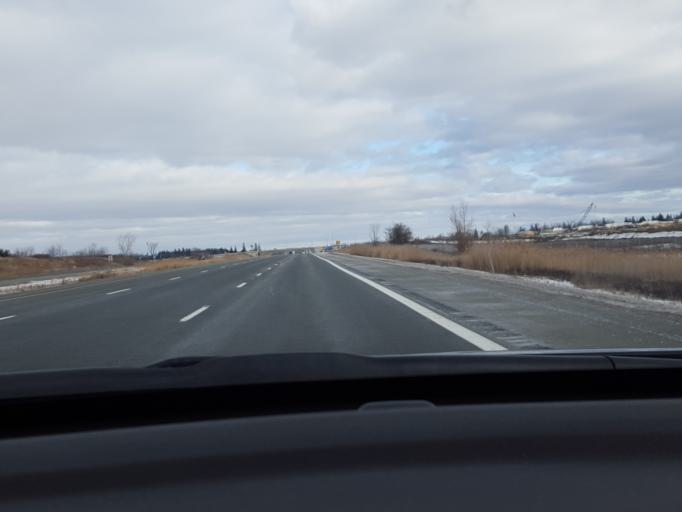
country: CA
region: Ontario
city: Markham
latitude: 43.8717
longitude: -79.2262
